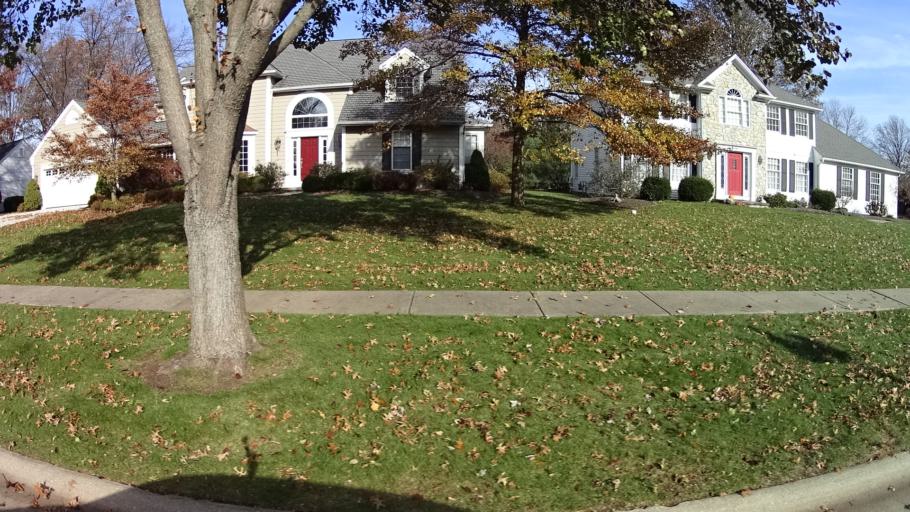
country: US
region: Ohio
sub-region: Lorain County
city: Avon Lake
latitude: 41.4954
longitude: -81.9810
